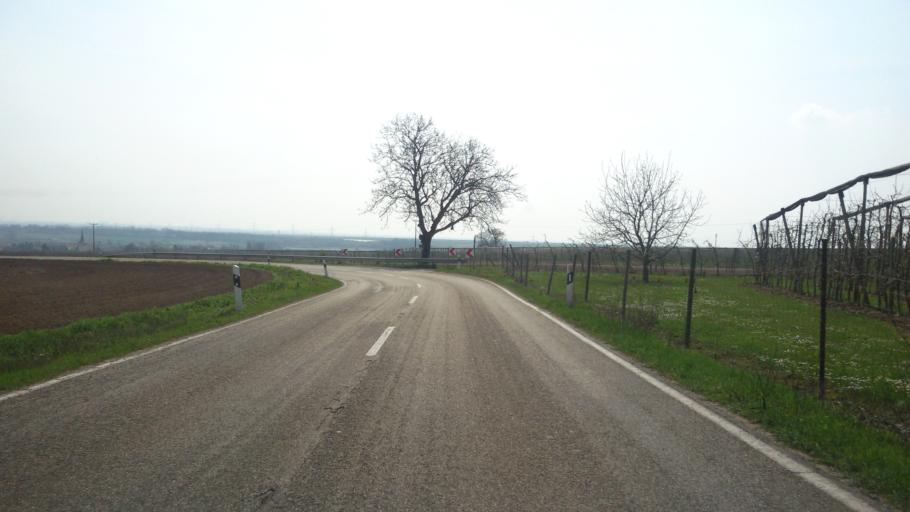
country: DE
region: Rheinland-Pfalz
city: Obersulzen
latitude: 49.5602
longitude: 8.2209
